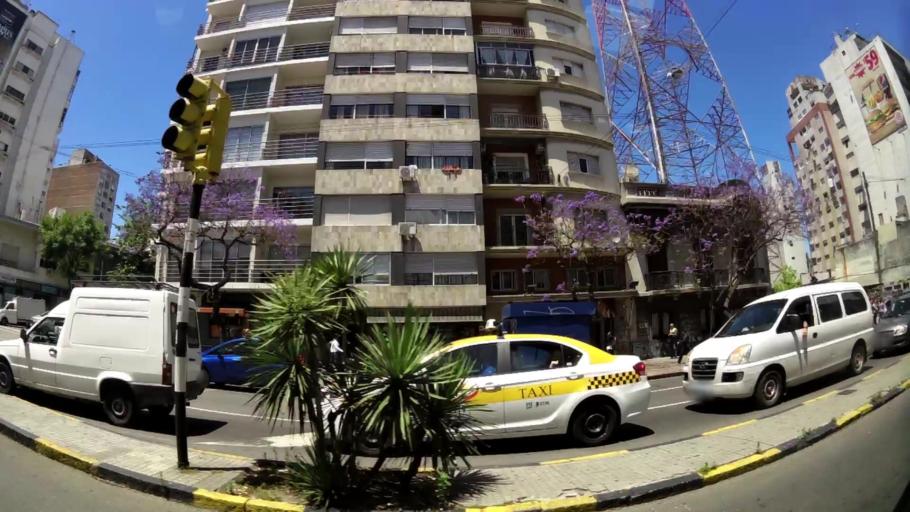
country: UY
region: Montevideo
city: Montevideo
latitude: -34.8981
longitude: -56.1662
